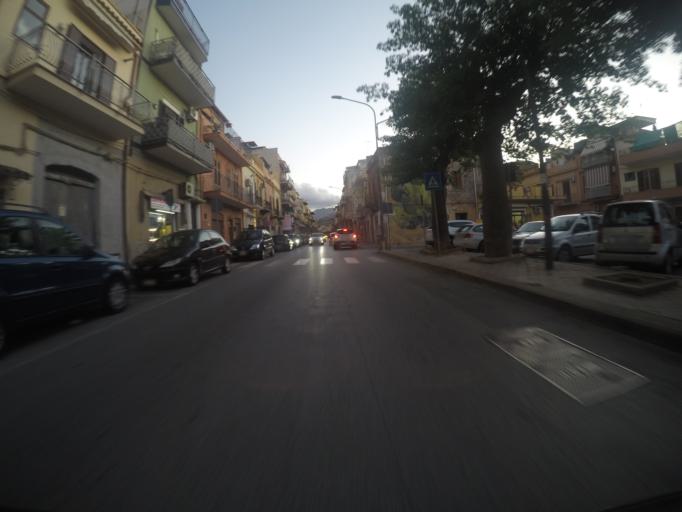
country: IT
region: Sicily
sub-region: Palermo
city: Capaci
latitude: 38.1751
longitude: 13.2418
